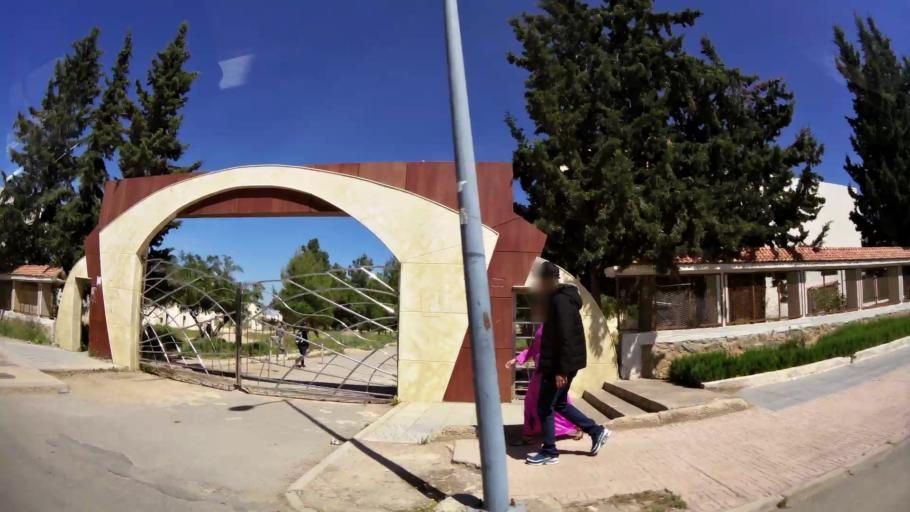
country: MA
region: Oriental
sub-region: Oujda-Angad
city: Oujda
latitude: 34.6508
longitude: -1.9014
